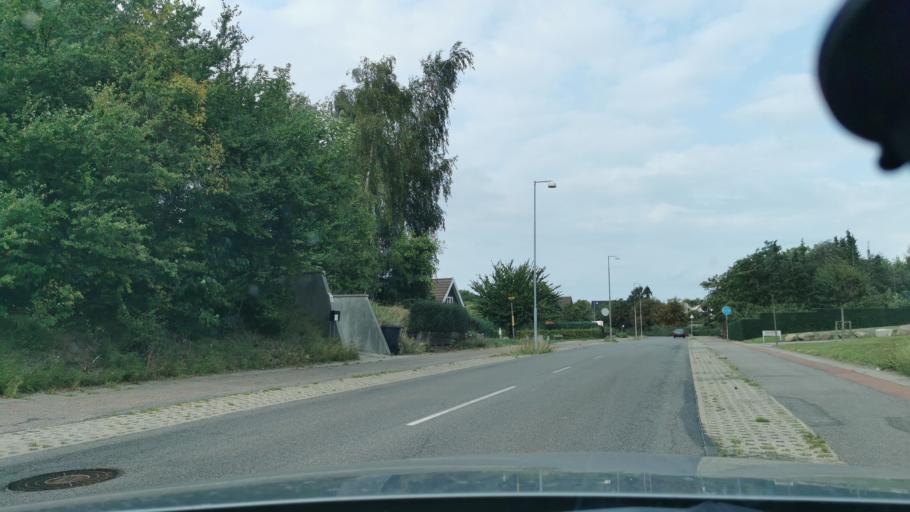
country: DK
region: Zealand
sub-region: Kalundborg Kommune
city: Kalundborg
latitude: 55.6935
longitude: 11.0635
